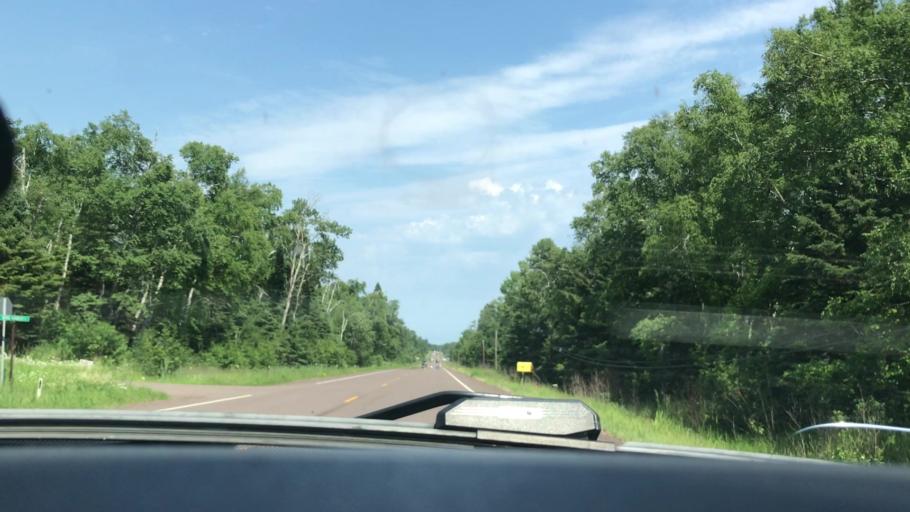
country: US
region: Minnesota
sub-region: Cook County
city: Grand Marais
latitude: 47.6421
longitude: -90.6955
